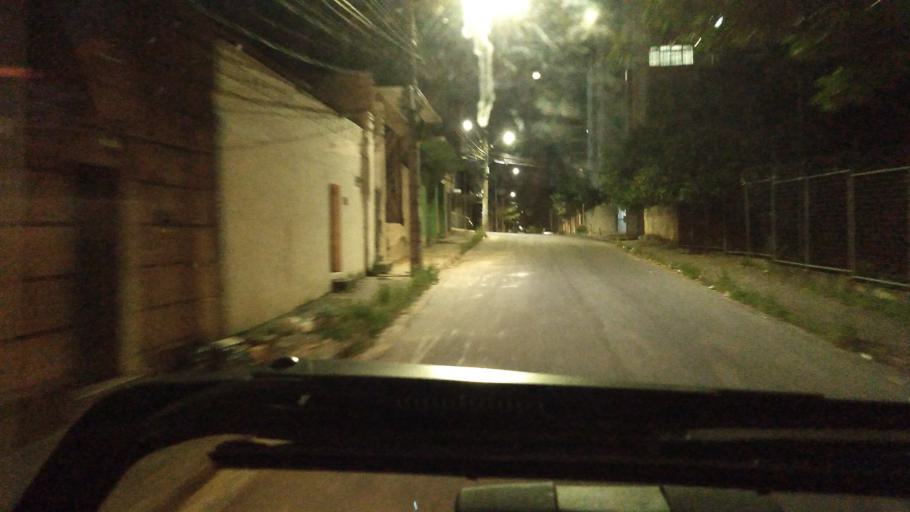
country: BR
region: Minas Gerais
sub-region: Belo Horizonte
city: Belo Horizonte
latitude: -19.9208
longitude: -43.9825
